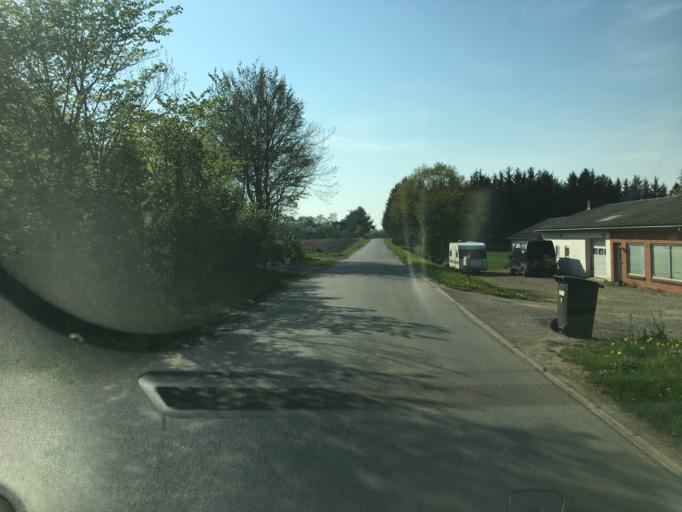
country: DK
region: South Denmark
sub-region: Haderslev Kommune
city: Vojens
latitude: 55.2323
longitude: 9.3374
